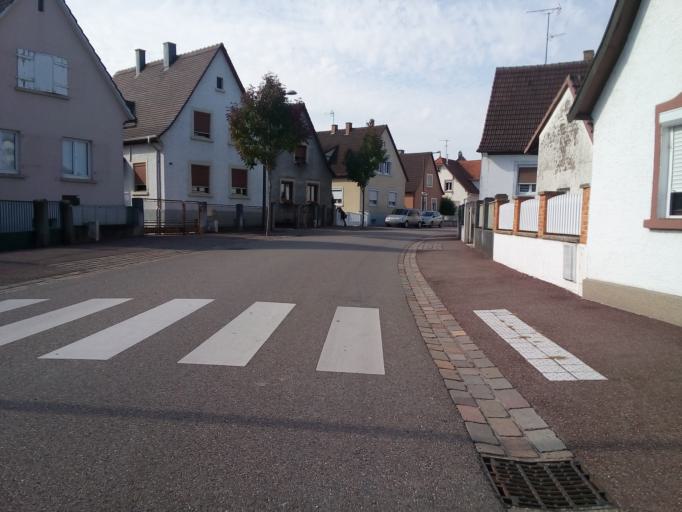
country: FR
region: Alsace
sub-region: Departement du Bas-Rhin
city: Drusenheim
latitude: 48.7587
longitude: 7.9541
